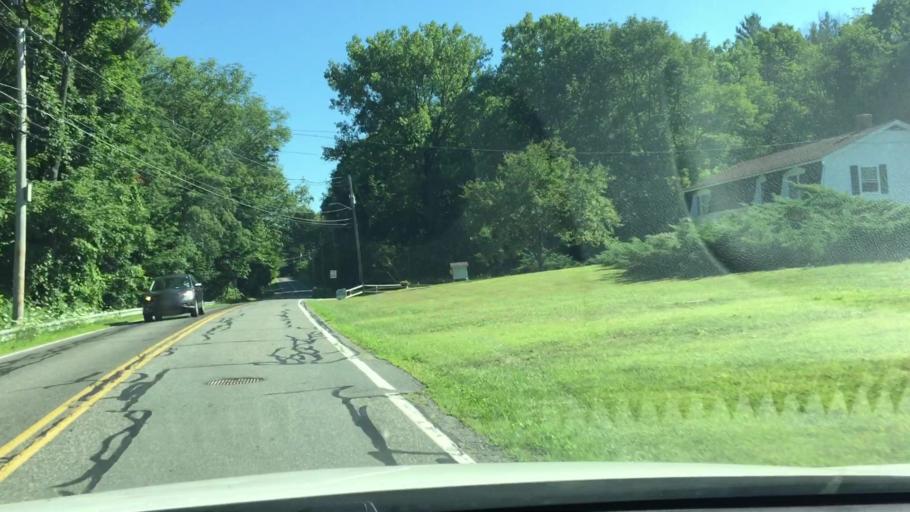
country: US
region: Massachusetts
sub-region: Berkshire County
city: West Stockbridge
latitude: 42.3406
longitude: -73.3666
